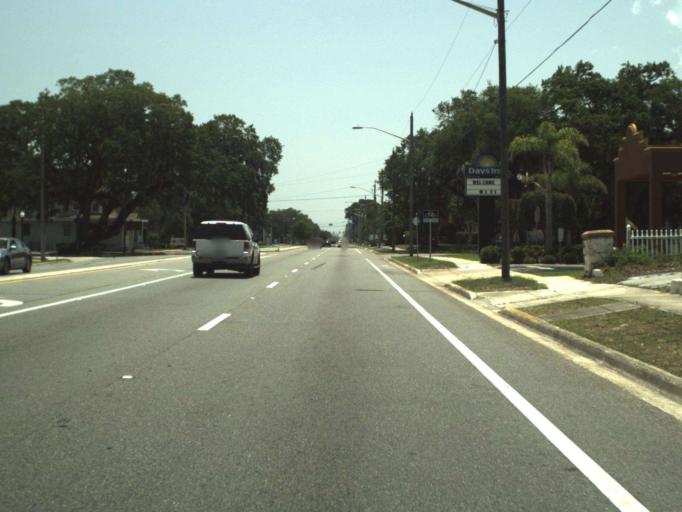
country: US
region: Florida
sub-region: Volusia County
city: Daytona Beach
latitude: 29.2020
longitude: -81.0182
